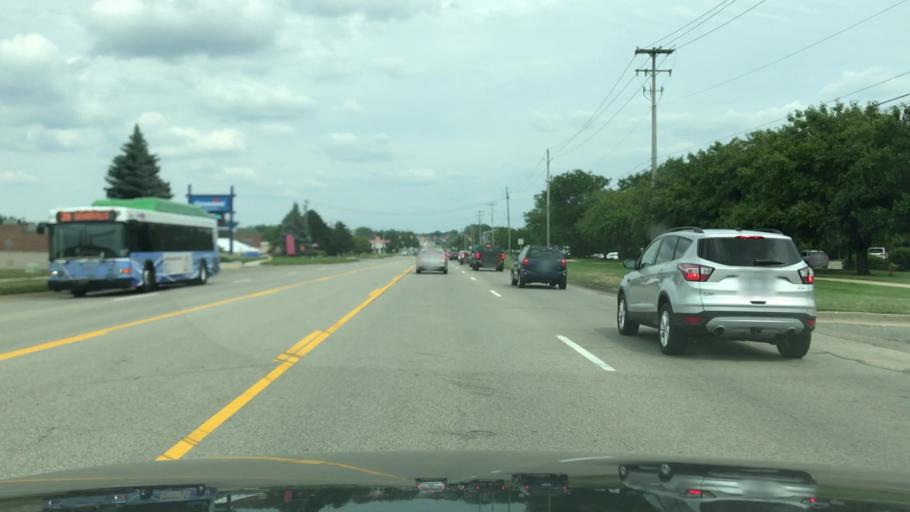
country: US
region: Michigan
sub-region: Kent County
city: East Grand Rapids
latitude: 42.9125
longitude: -85.5624
